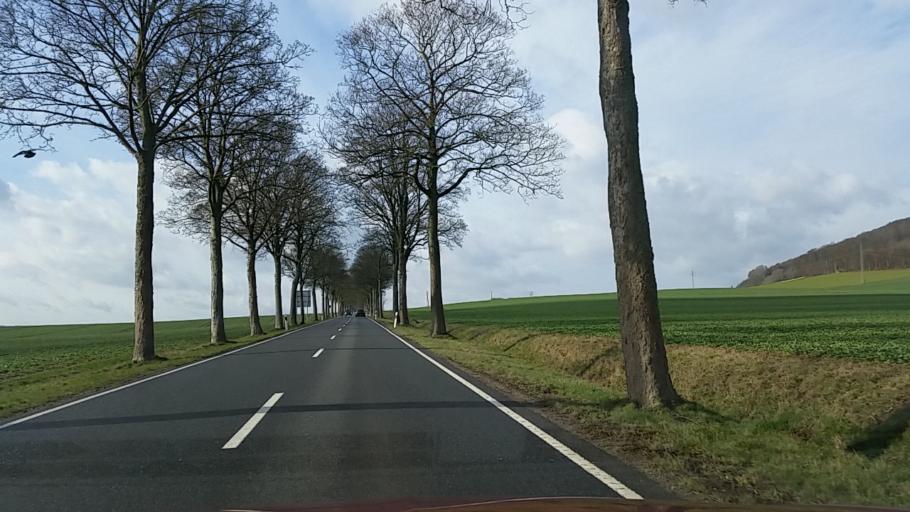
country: DE
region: Lower Saxony
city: Kalefeld
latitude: 51.8109
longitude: 10.0945
